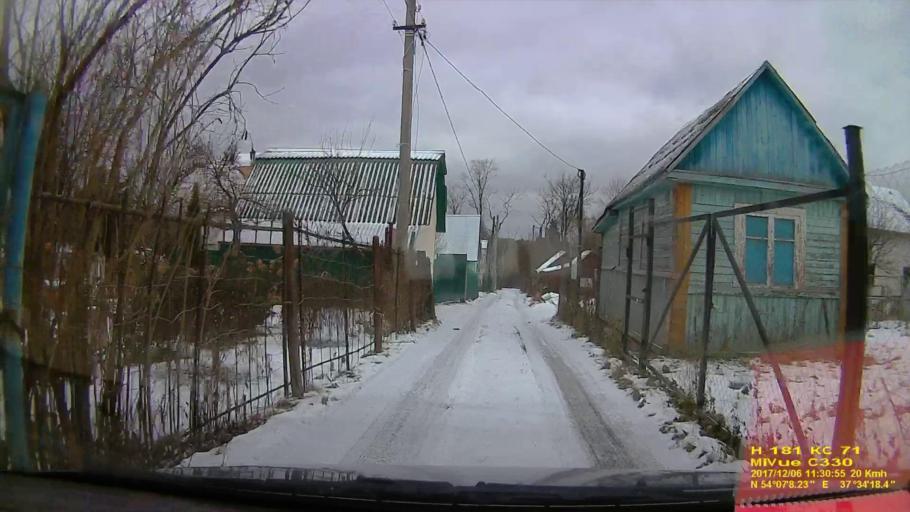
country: RU
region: Tula
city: Mendeleyevskiy
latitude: 54.1189
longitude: 37.5717
